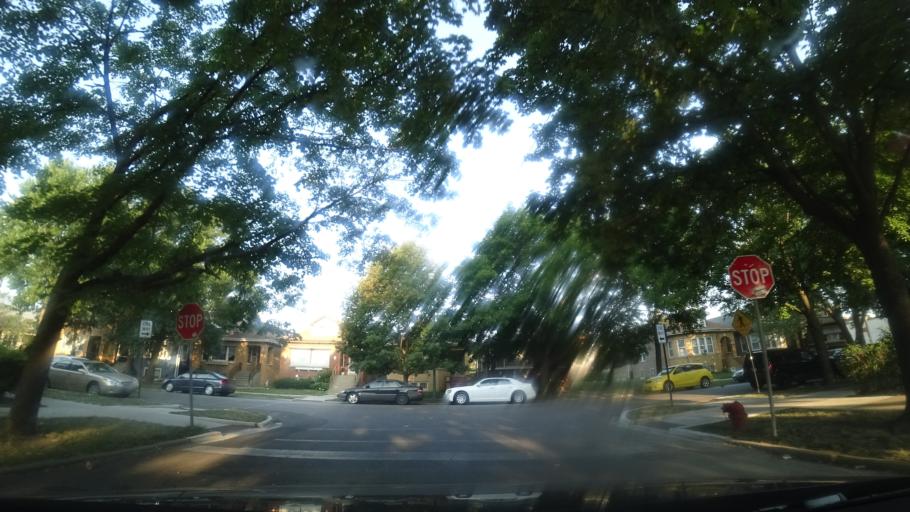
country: US
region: Illinois
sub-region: Cook County
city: Elmwood Park
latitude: 41.9378
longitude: -87.7613
